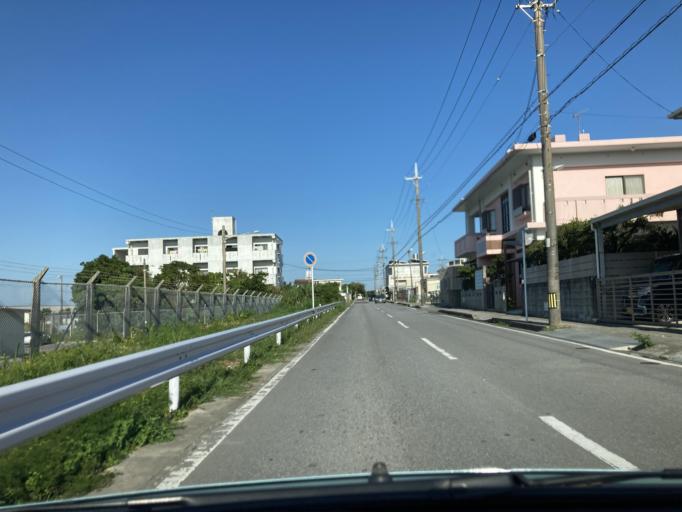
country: JP
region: Okinawa
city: Ginowan
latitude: 26.2656
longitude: 127.7559
